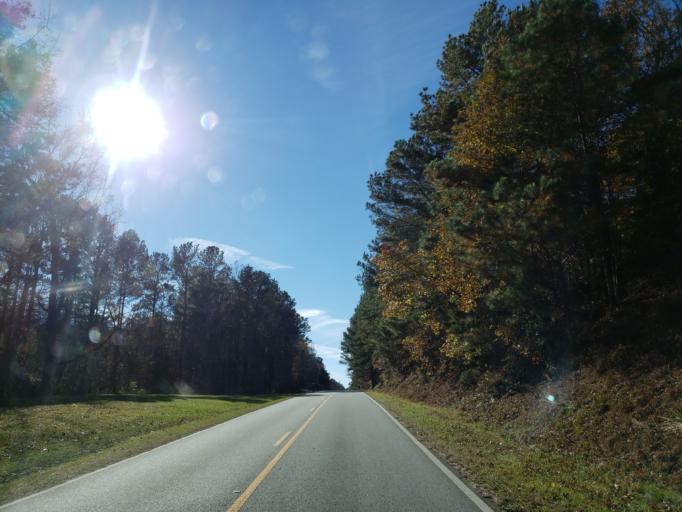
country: US
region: Alabama
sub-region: Cleburne County
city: Heflin
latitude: 33.5966
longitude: -85.6233
